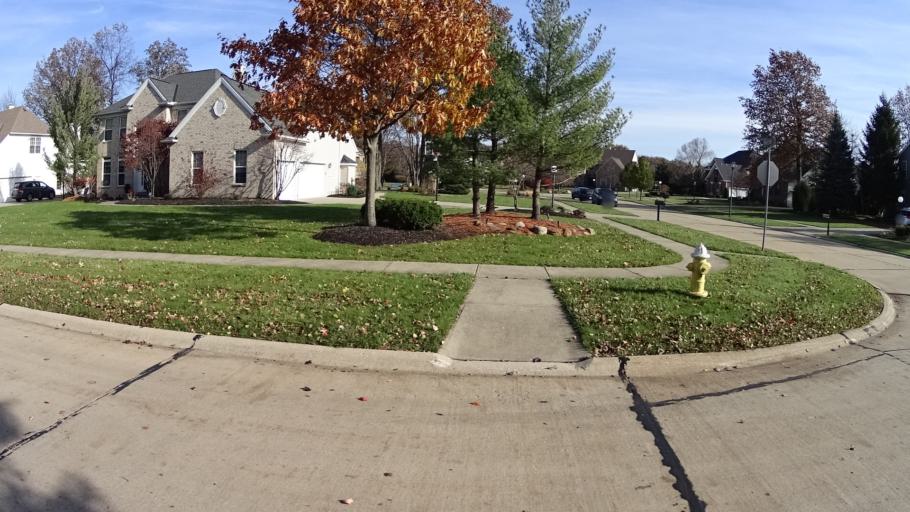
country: US
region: Ohio
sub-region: Cuyahoga County
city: Bay Village
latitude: 41.4962
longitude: -81.9734
